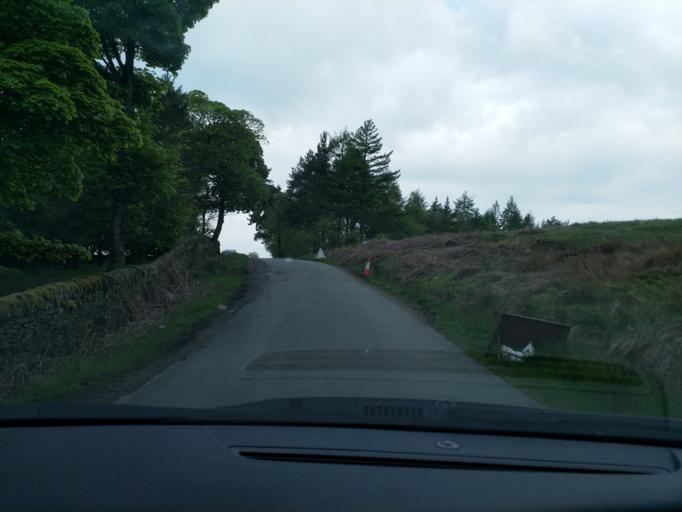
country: GB
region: England
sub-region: Derbyshire
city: Hathersage
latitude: 53.3493
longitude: -1.6418
